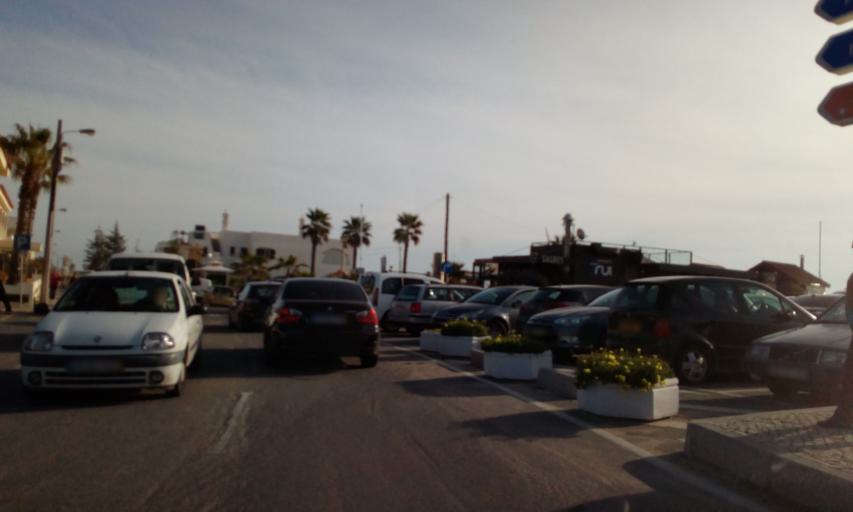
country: PT
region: Faro
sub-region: Faro
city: Faro
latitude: 37.0081
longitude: -7.9947
